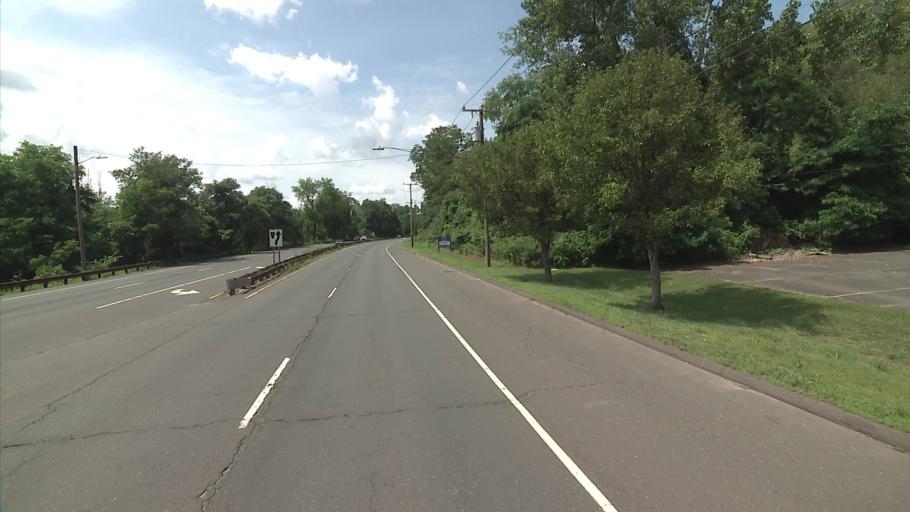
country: US
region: Connecticut
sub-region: Middlesex County
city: Portland
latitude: 41.5720
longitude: -72.6150
